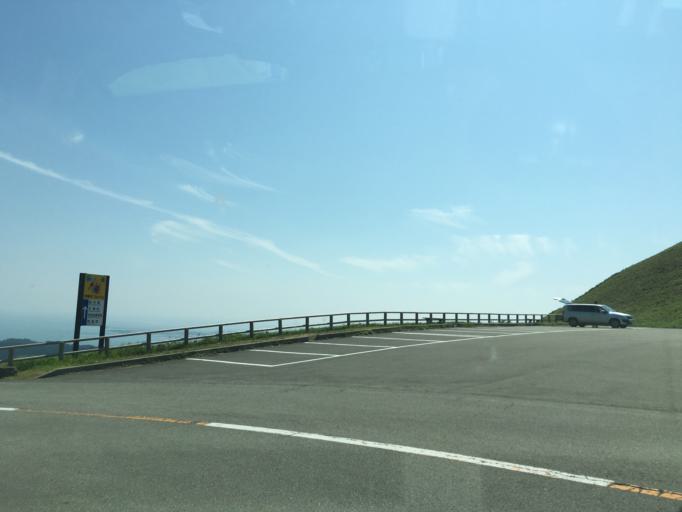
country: JP
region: Akita
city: Tenno
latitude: 39.9305
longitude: 139.8724
